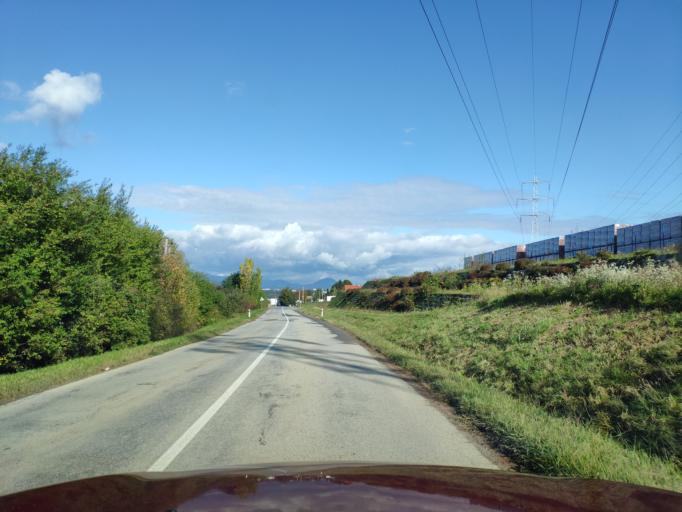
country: SK
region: Presovsky
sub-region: Okres Presov
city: Presov
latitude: 48.9054
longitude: 21.2621
